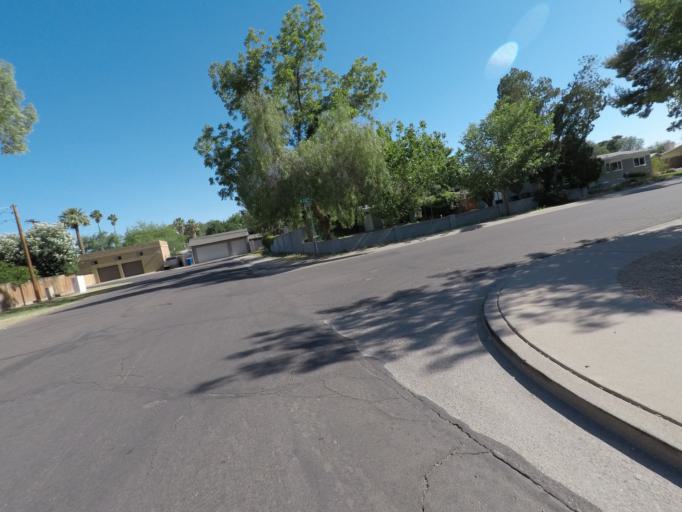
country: US
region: Arizona
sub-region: Maricopa County
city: Tempe Junction
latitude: 33.4187
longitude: -111.9480
